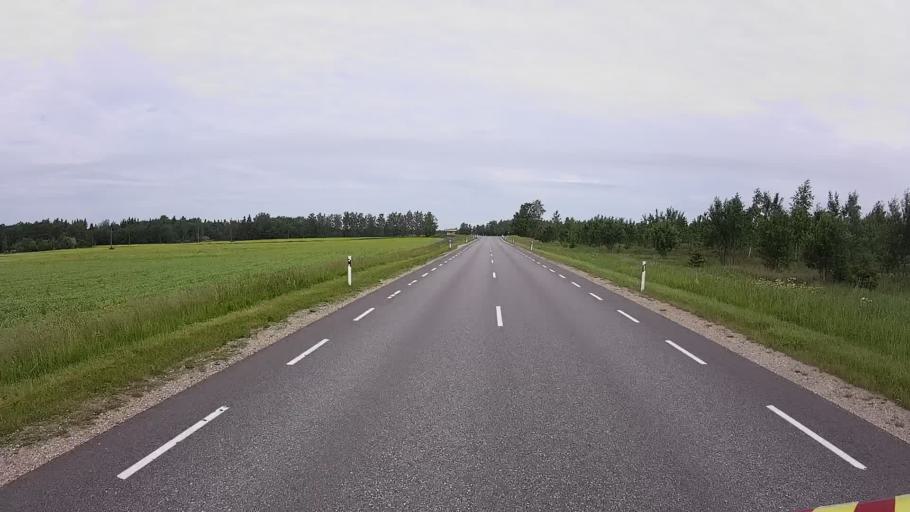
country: EE
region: Viljandimaa
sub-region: Karksi vald
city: Karksi-Nuia
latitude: 58.1550
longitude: 25.5955
